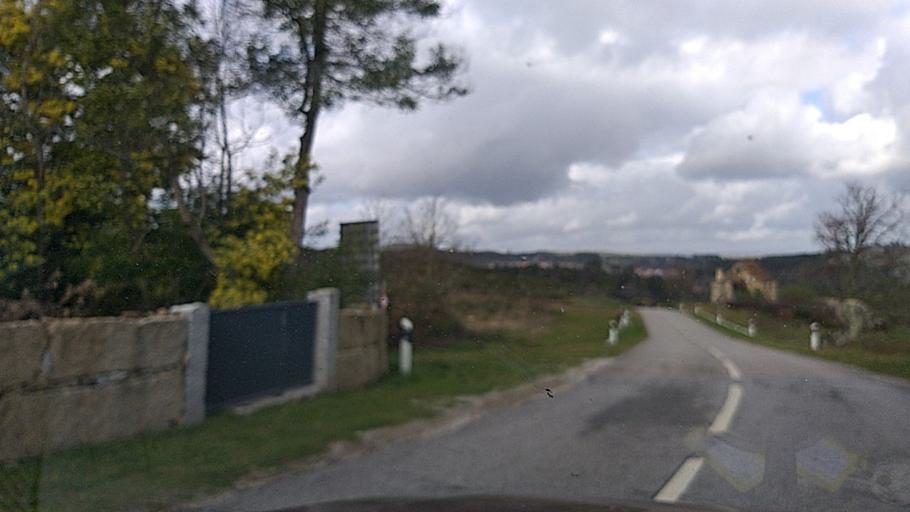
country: PT
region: Guarda
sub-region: Fornos de Algodres
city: Fornos de Algodres
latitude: 40.6539
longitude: -7.5503
